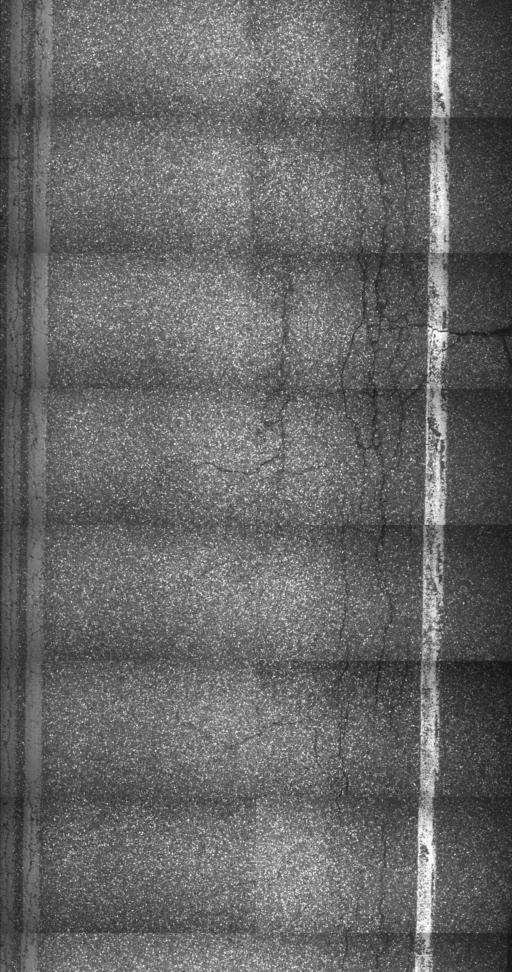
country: US
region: Vermont
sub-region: Rutland County
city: Brandon
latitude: 43.8363
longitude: -73.0414
